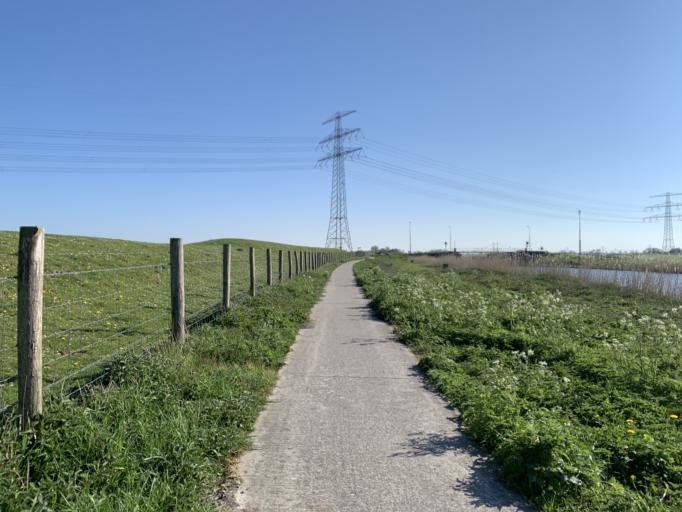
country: NL
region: Groningen
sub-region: Gemeente Winsum
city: Winsum
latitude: 53.2935
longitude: 6.5048
